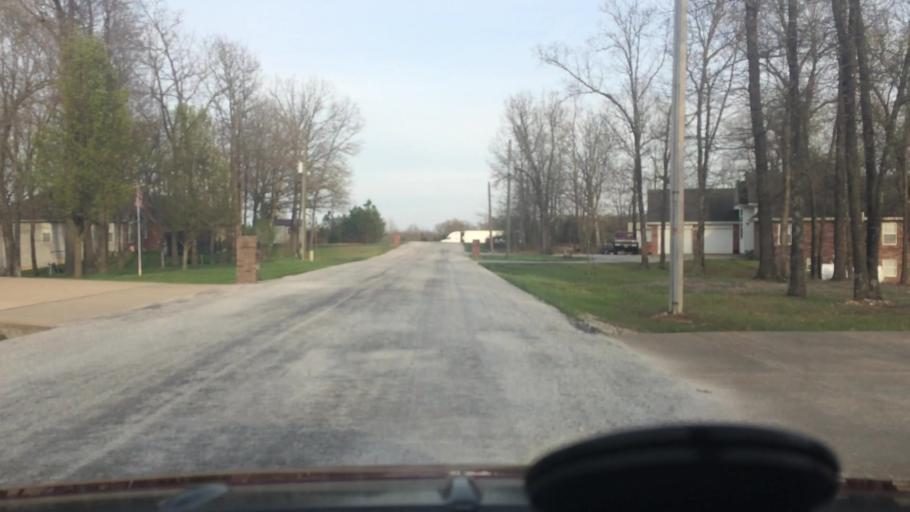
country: US
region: Missouri
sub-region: Greene County
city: Strafford
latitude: 37.2820
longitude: -93.0459
